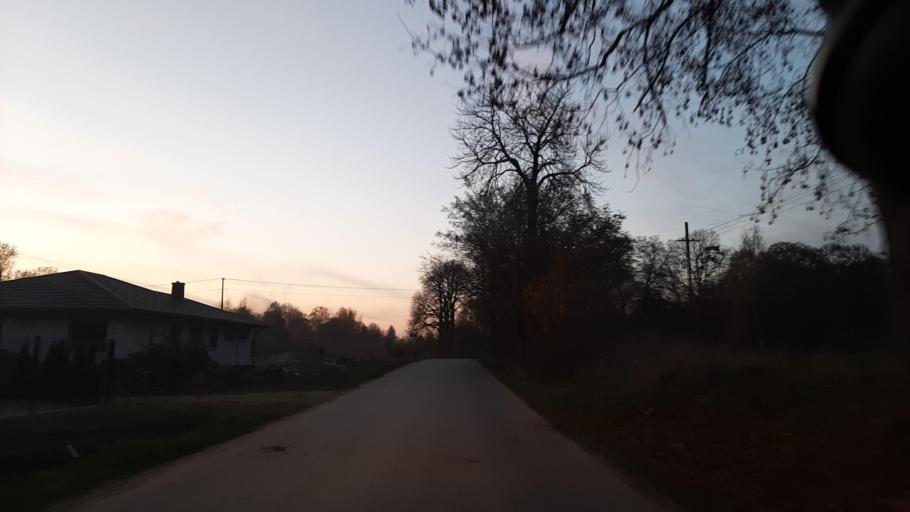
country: PL
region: Lublin Voivodeship
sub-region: Powiat lubelski
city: Jastkow
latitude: 51.3393
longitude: 22.4193
